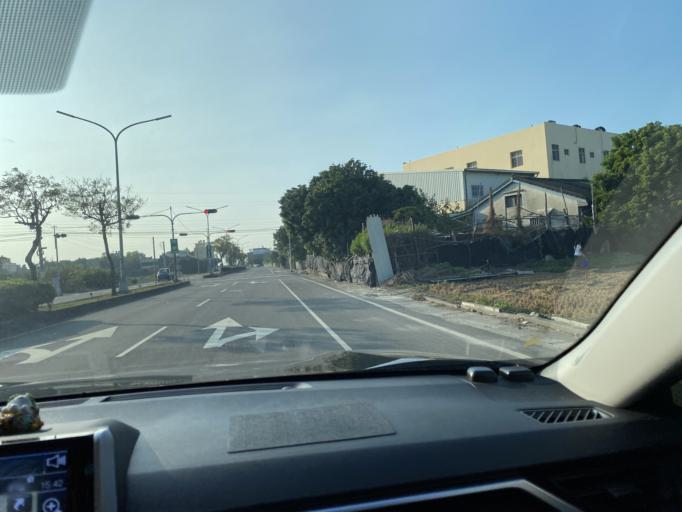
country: TW
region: Taiwan
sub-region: Changhua
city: Chang-hua
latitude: 23.9529
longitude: 120.4228
